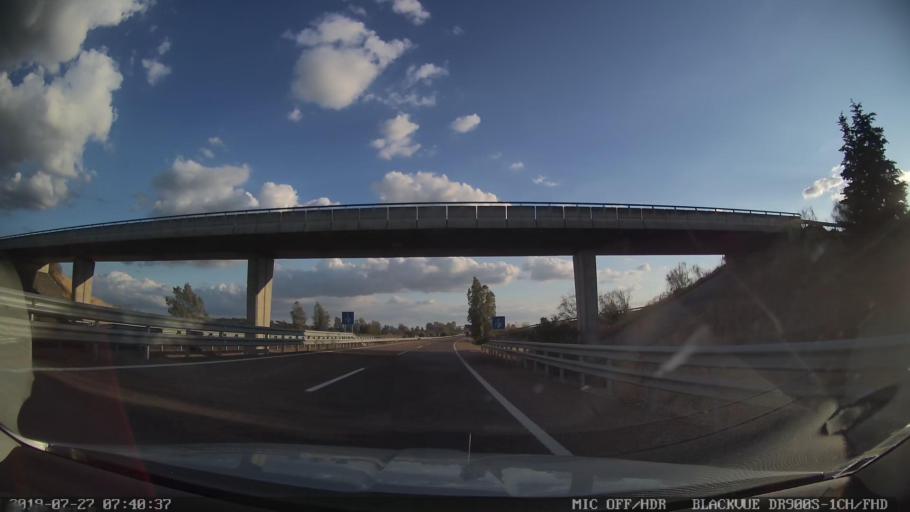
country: ES
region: Extremadura
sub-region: Provincia de Badajoz
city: Santa Amalia
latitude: 39.0429
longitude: -6.0613
